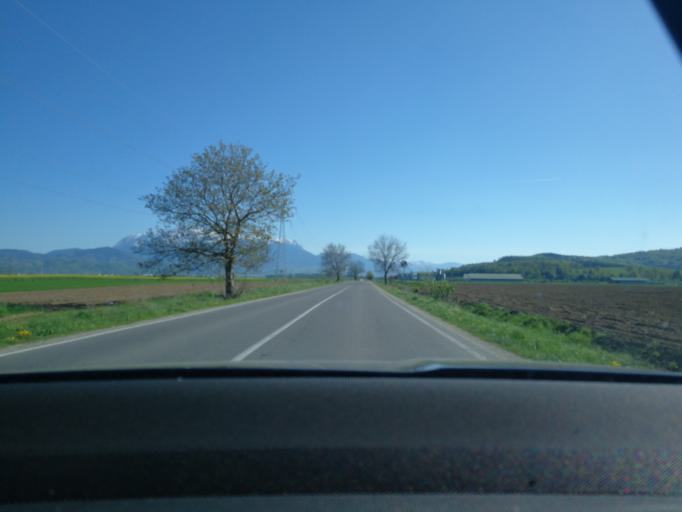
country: RO
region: Brasov
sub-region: Comuna Vulcan
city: Vulcan
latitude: 45.6265
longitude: 25.4268
